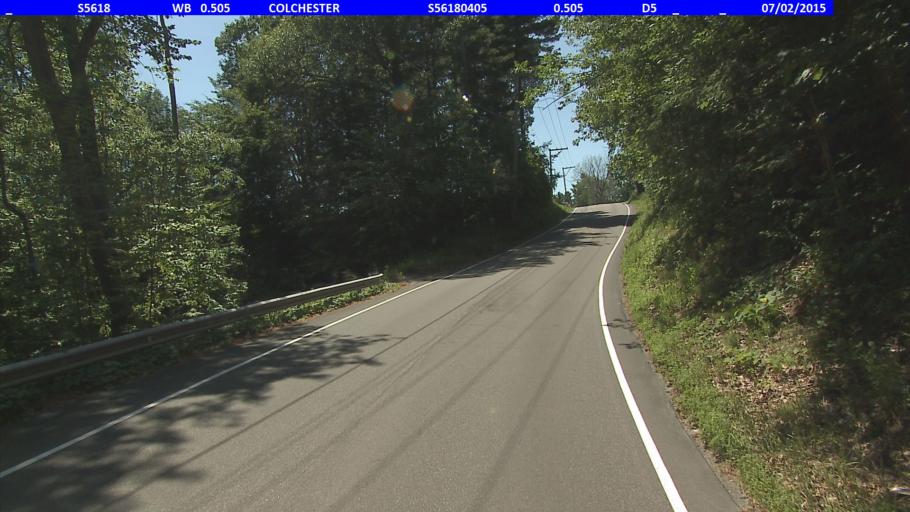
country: US
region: Vermont
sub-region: Chittenden County
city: Colchester
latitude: 44.5462
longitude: -73.2058
